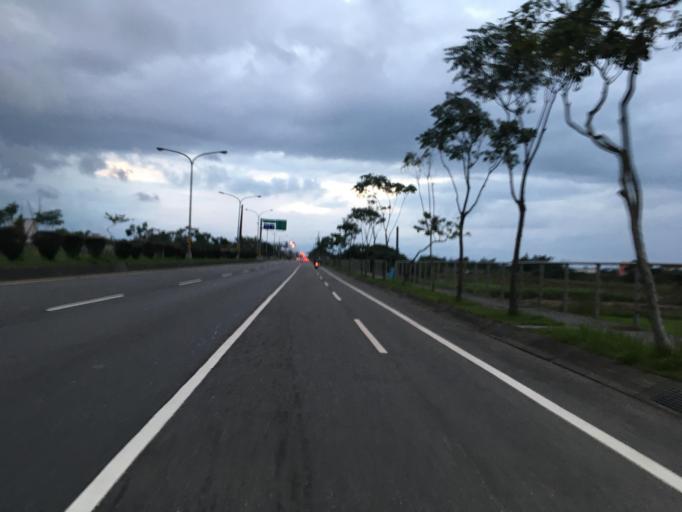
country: TW
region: Taiwan
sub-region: Yilan
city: Yilan
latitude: 24.6161
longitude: 121.8479
